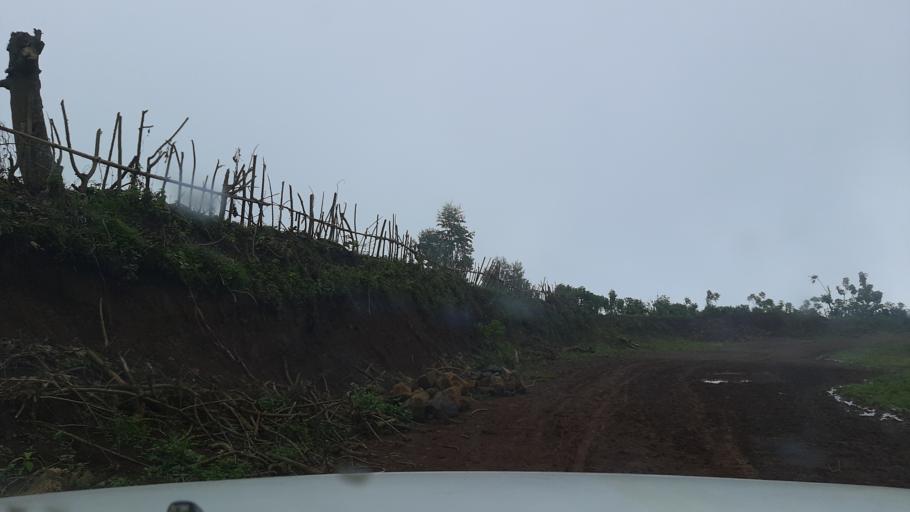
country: ET
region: Southern Nations, Nationalities, and People's Region
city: Bonga
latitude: 7.1168
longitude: 36.5665
